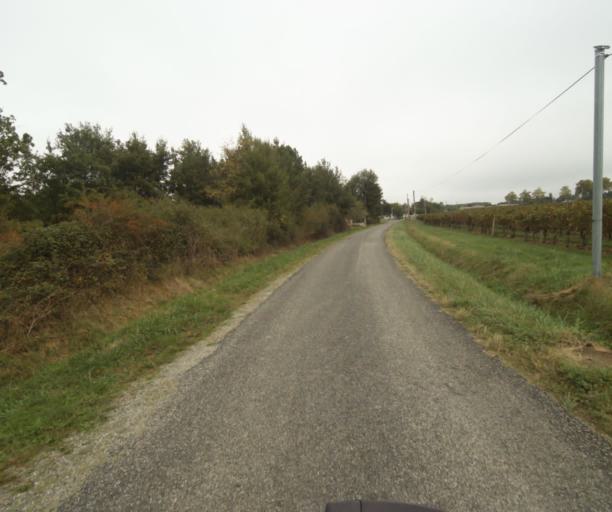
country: FR
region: Midi-Pyrenees
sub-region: Departement du Tarn-et-Garonne
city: Labastide-Saint-Pierre
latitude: 43.8827
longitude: 1.3717
